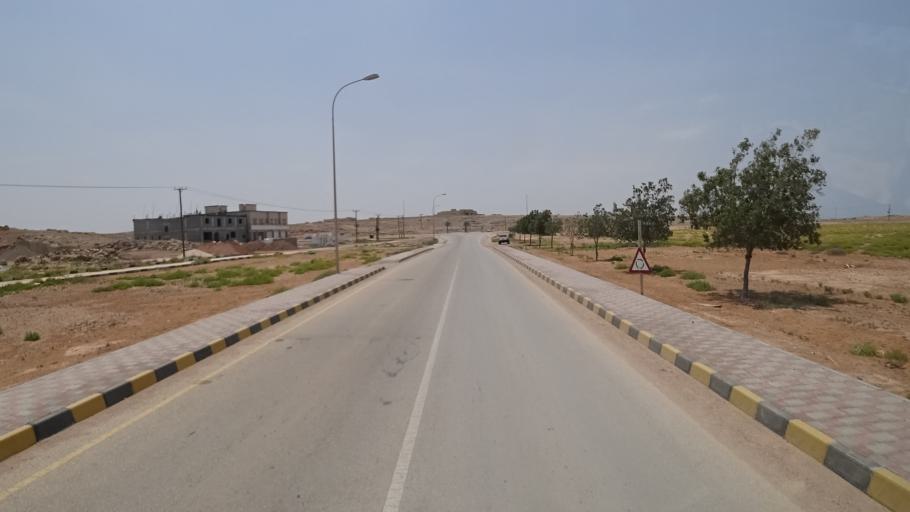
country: OM
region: Ash Sharqiyah
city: Sur
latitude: 22.5097
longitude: 59.7967
